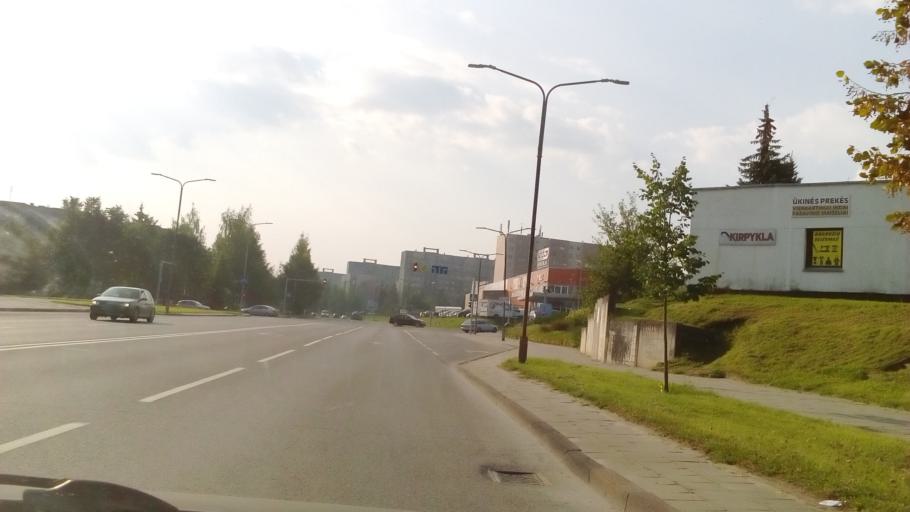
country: LT
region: Alytaus apskritis
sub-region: Alytus
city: Alytus
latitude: 54.3949
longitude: 24.0174
